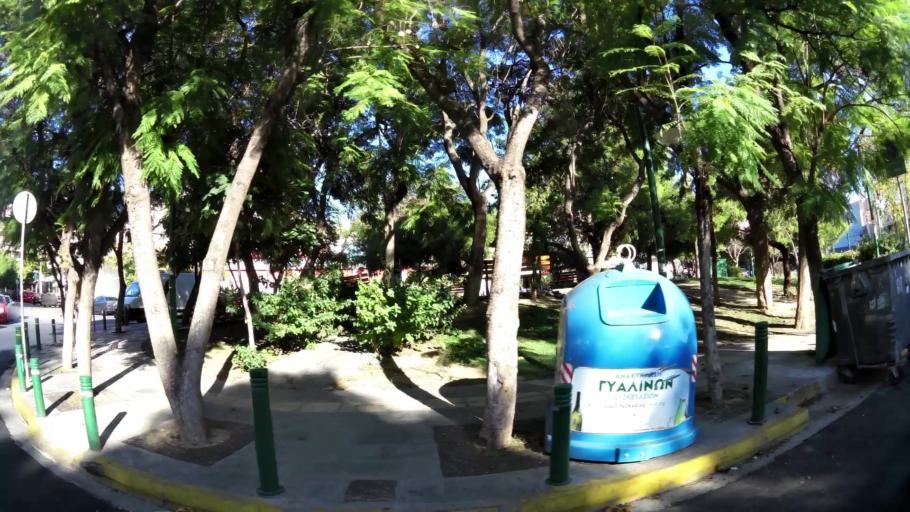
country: GR
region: Attica
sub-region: Nomos Piraios
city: Perama
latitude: 37.9647
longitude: 23.5620
